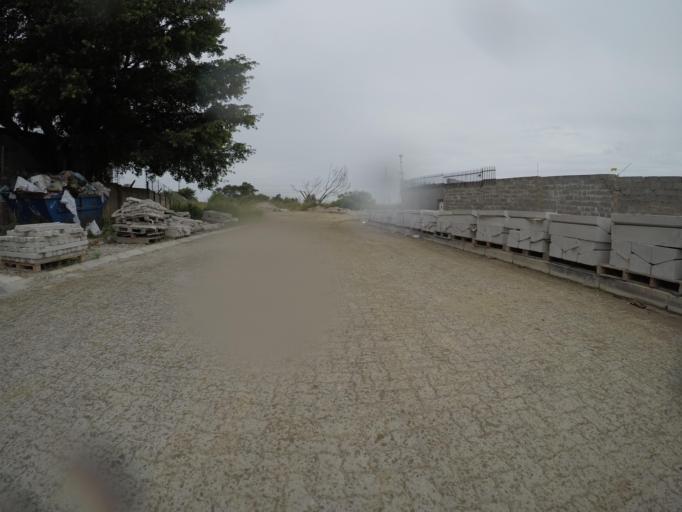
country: ZA
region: Eastern Cape
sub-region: Buffalo City Metropolitan Municipality
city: East London
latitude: -32.9923
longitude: 27.8310
